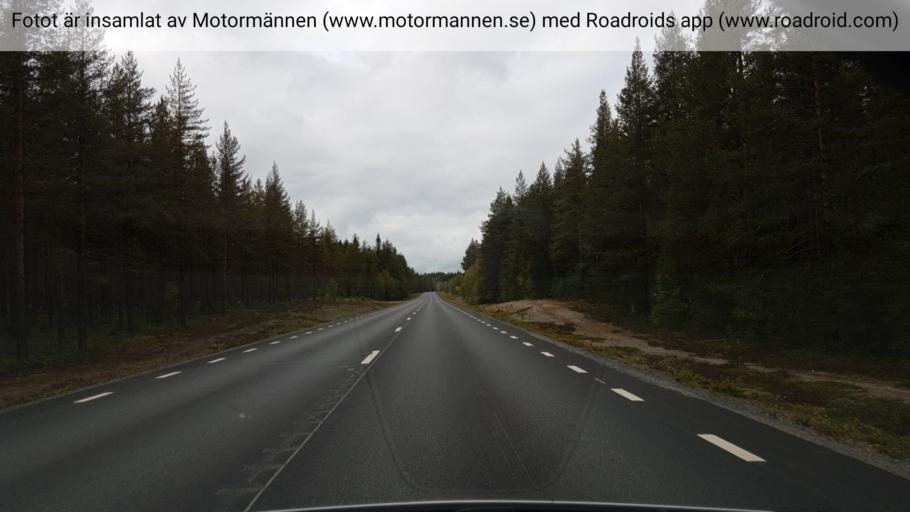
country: SE
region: Vaesterbotten
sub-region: Norsjo Kommun
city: Norsjoe
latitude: 64.9801
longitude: 19.5886
